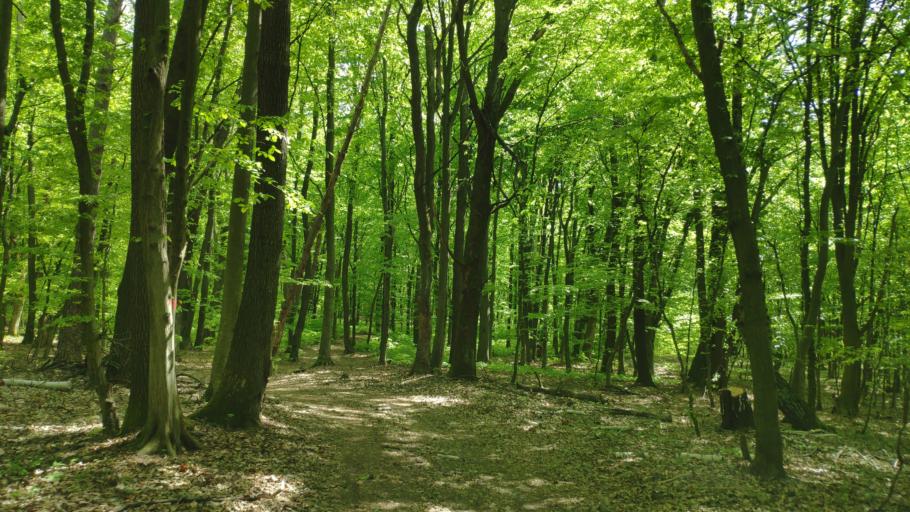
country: SK
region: Kosicky
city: Kosice
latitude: 48.6634
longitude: 21.4311
